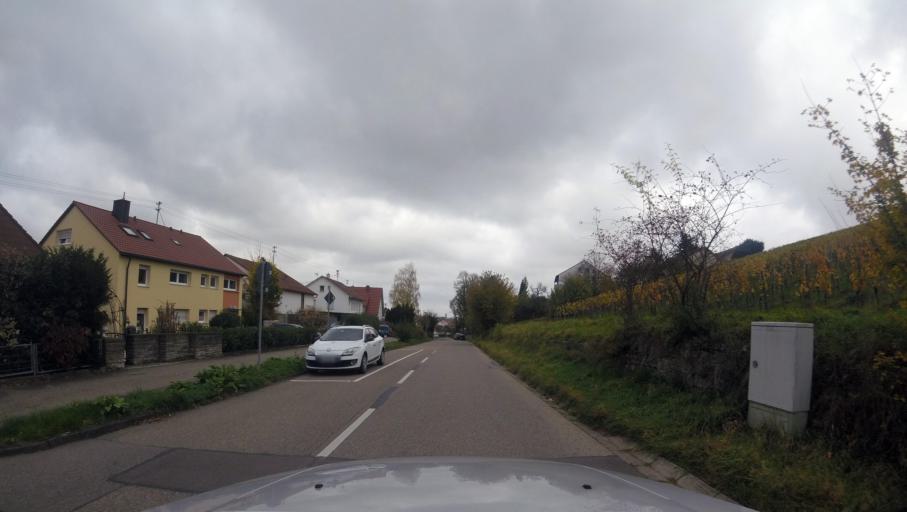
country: DE
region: Baden-Wuerttemberg
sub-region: Regierungsbezirk Stuttgart
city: Winnenden
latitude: 48.8671
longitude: 9.4021
